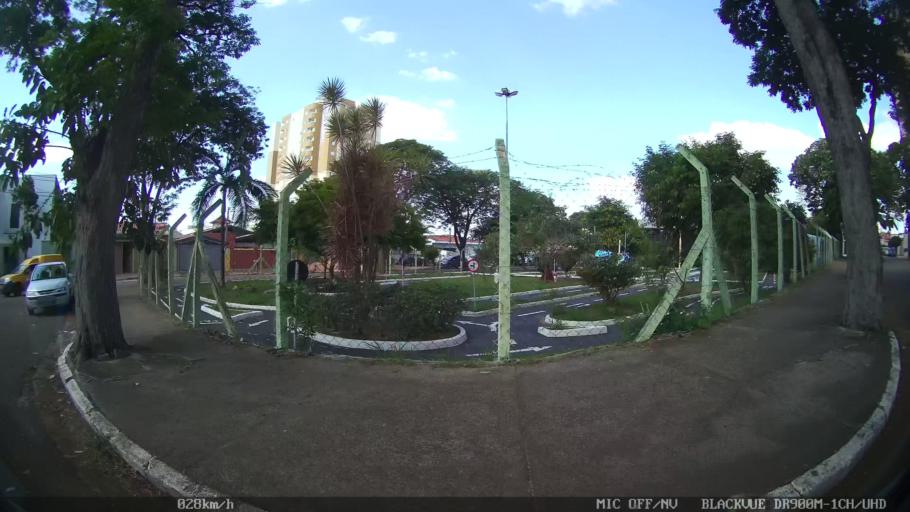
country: BR
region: Sao Paulo
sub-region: Sumare
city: Sumare
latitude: -22.8265
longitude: -47.2649
